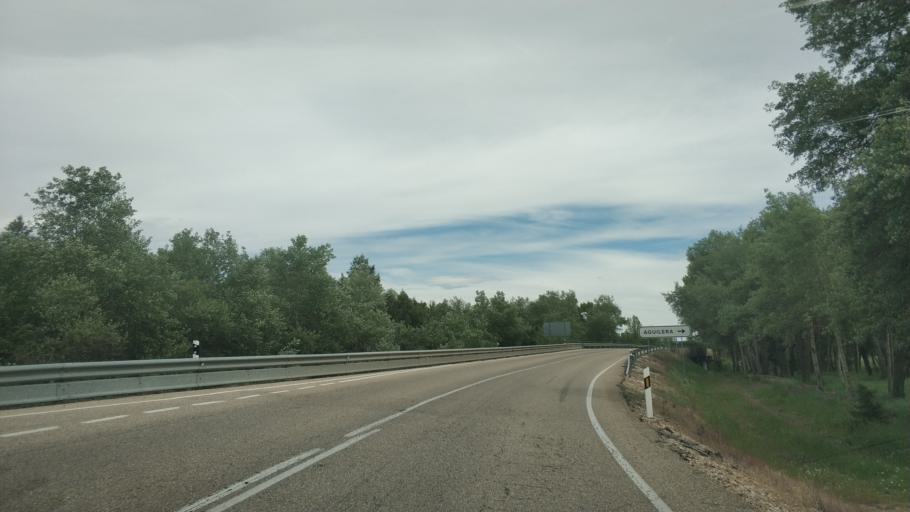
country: ES
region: Castille and Leon
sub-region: Provincia de Soria
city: Bayubas de Abajo
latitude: 41.5039
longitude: -2.8895
